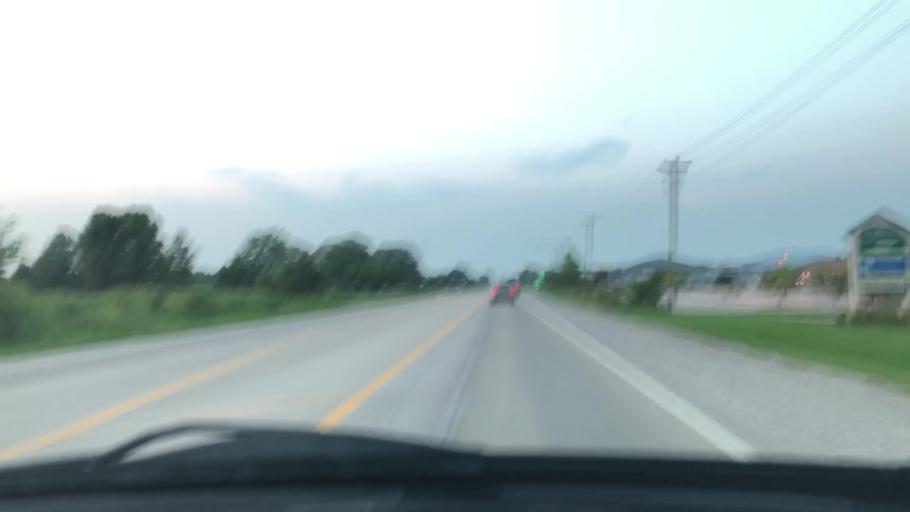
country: US
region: Iowa
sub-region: Johnson County
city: North Liberty
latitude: 41.7296
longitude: -91.6077
